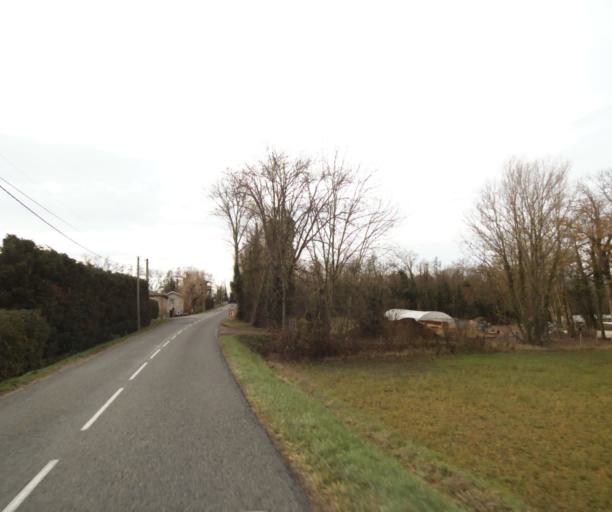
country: FR
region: Rhone-Alpes
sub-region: Departement de la Loire
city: Saint-Marcellin-en-Forez
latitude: 45.5139
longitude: 4.1791
